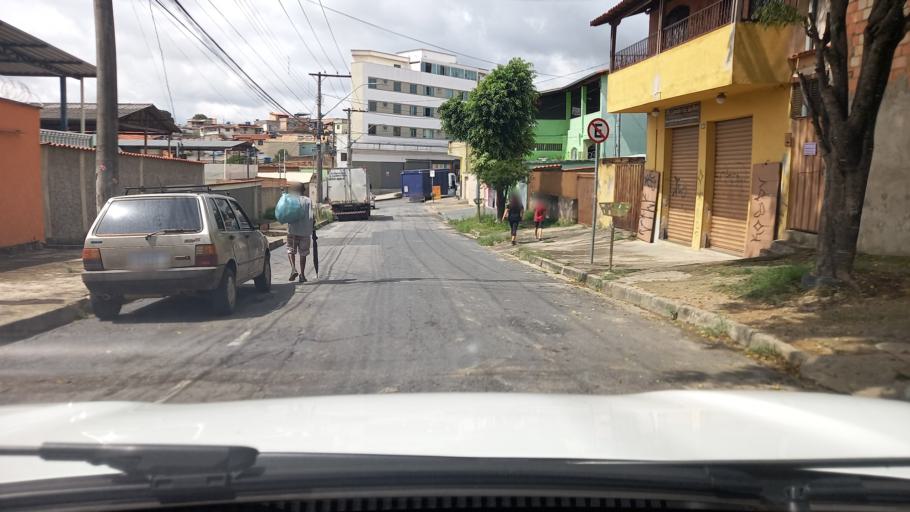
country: BR
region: Minas Gerais
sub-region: Contagem
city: Contagem
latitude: -19.9006
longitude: -44.0260
